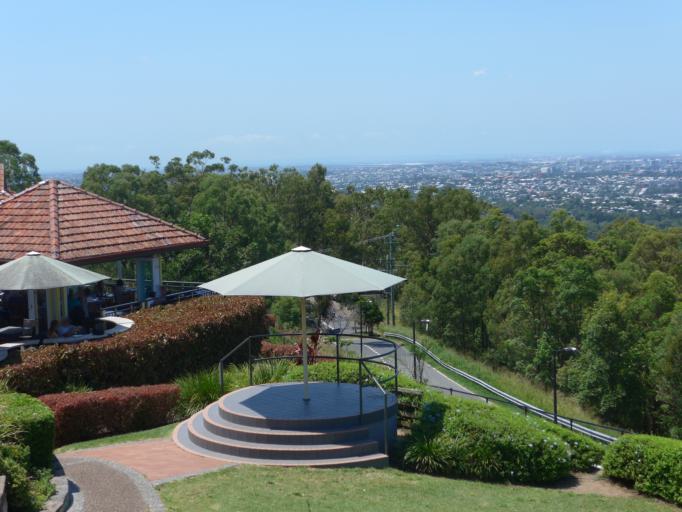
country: AU
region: Queensland
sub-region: Brisbane
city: Taringa
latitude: -27.4850
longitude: 152.9592
